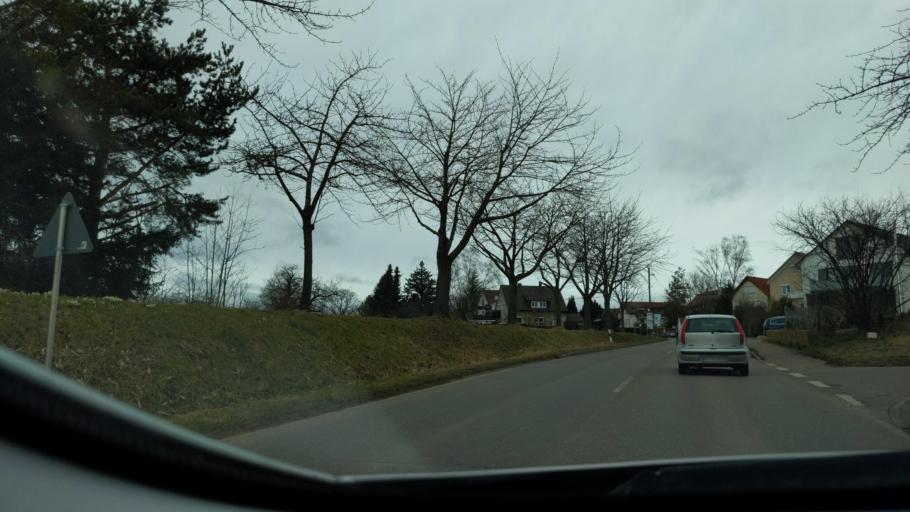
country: DE
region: Baden-Wuerttemberg
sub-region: Regierungsbezirk Stuttgart
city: Ostfildern
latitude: 48.7236
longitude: 9.2565
